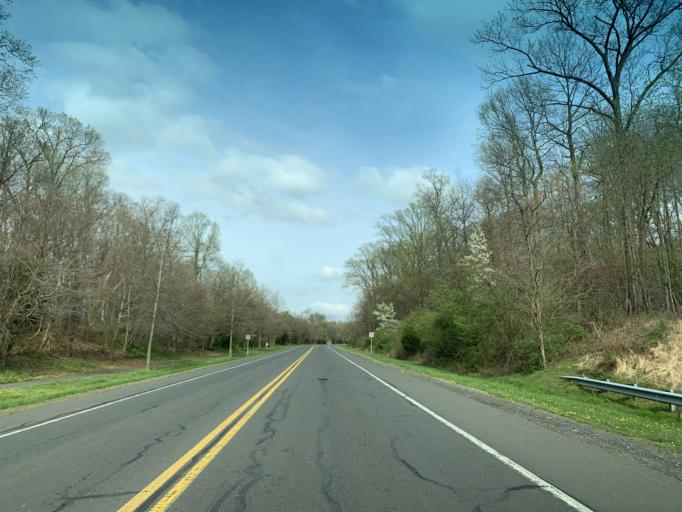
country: US
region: Maryland
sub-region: Montgomery County
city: Cloverly
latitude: 39.1220
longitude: -77.0063
